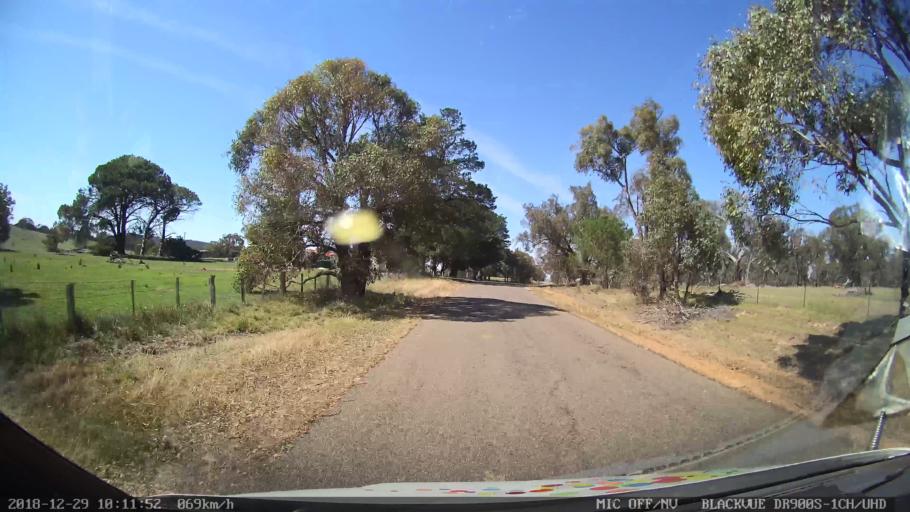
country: AU
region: New South Wales
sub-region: Yass Valley
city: Gundaroo
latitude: -34.8883
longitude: 149.4508
